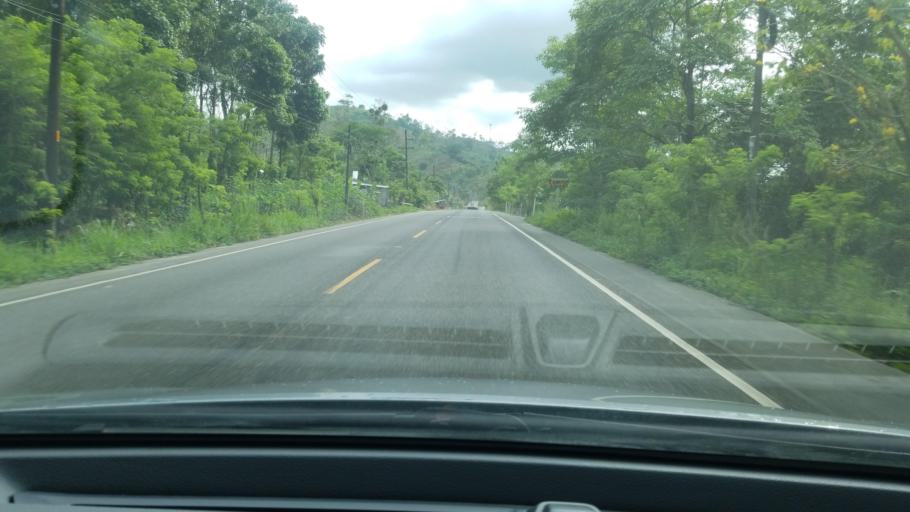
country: HN
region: Cortes
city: Potrerillos
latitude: 15.5947
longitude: -88.3053
